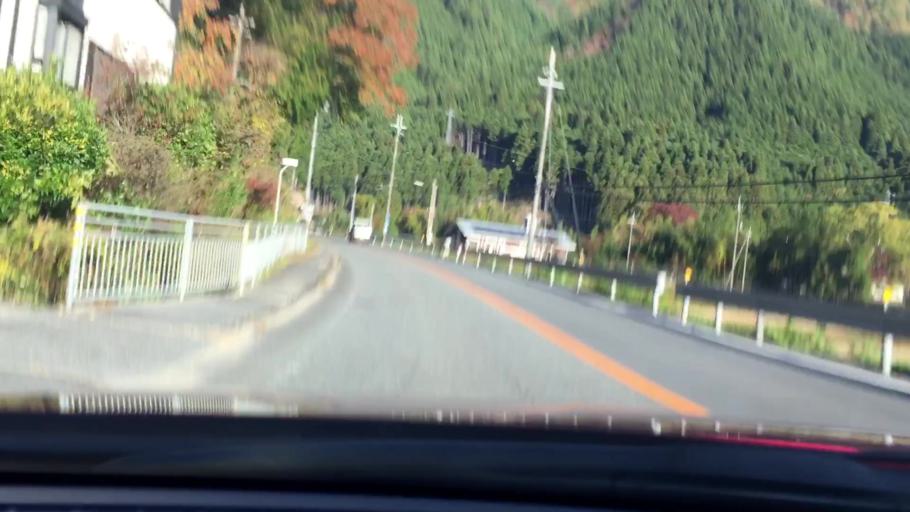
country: JP
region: Hyogo
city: Yamazakicho-nakabirose
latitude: 35.1381
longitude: 134.5561
